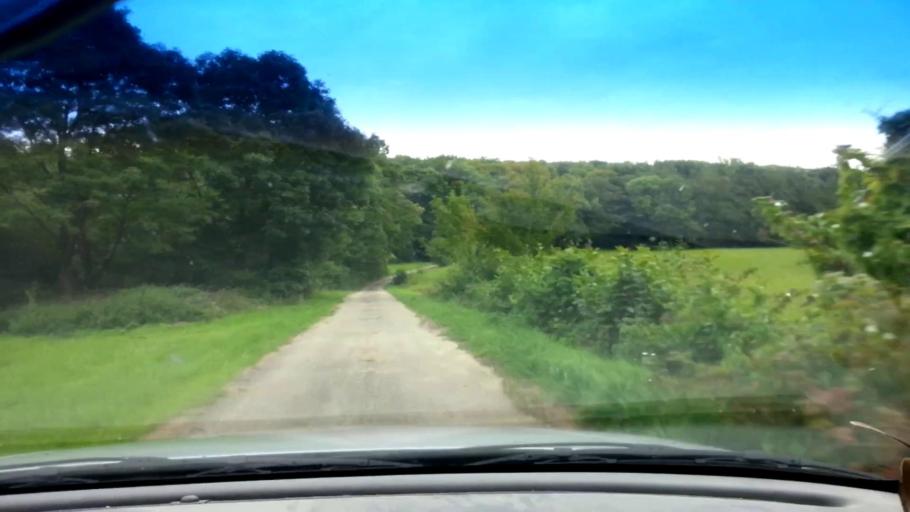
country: DE
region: Bavaria
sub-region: Upper Franconia
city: Litzendorf
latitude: 49.9320
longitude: 11.0276
